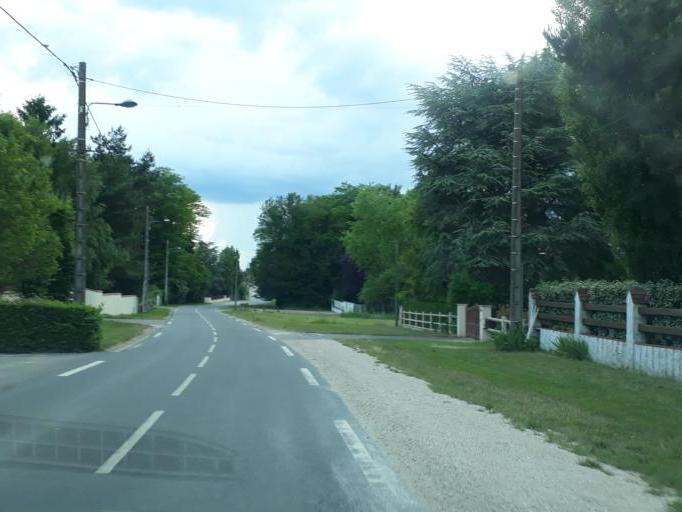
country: FR
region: Centre
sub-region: Departement du Loiret
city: Ormes
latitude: 47.9188
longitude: 1.7960
